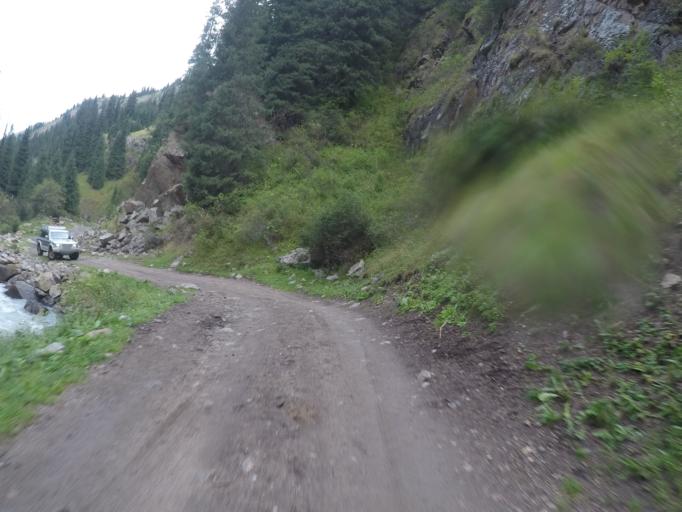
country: KG
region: Ysyk-Koel
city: Teploklyuchenka
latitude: 42.4162
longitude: 78.5723
